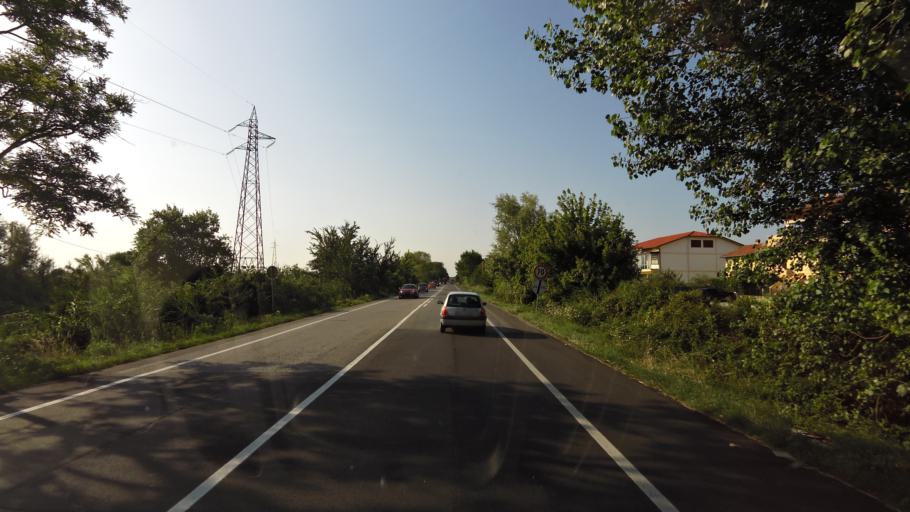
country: IT
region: Emilia-Romagna
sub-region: Provincia di Ravenna
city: Cervia
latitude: 44.2430
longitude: 12.3522
